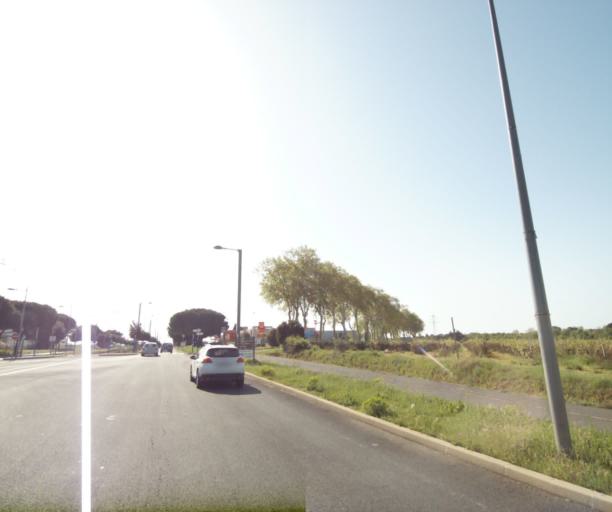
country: FR
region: Languedoc-Roussillon
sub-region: Departement de l'Herault
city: Perols
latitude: 43.5796
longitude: 3.9318
